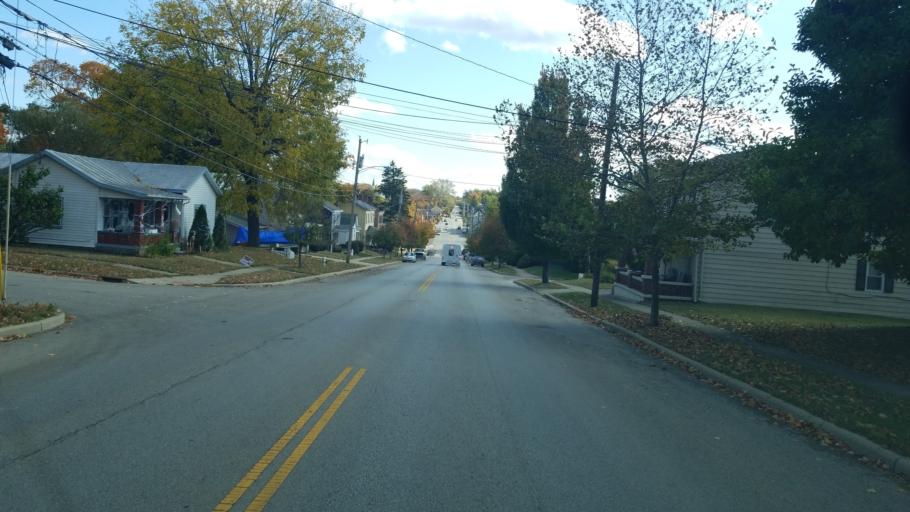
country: US
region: Ohio
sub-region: Warren County
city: Lebanon
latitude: 39.4359
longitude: -84.2130
